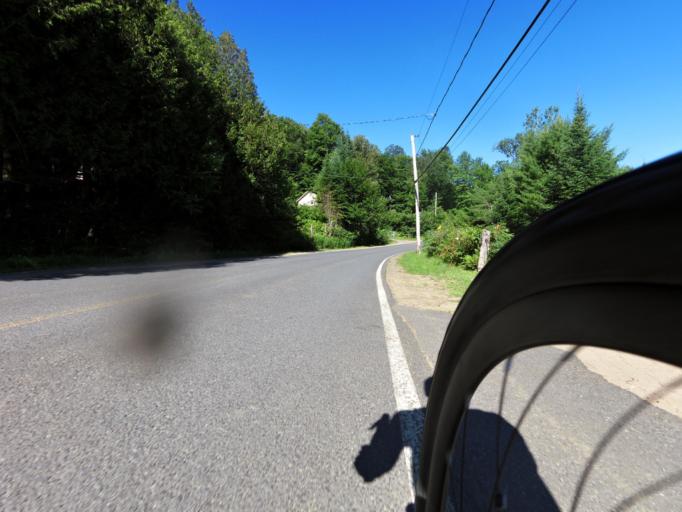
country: CA
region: Quebec
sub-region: Laurentides
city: Brownsburg-Chatham
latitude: 45.8940
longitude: -74.6001
